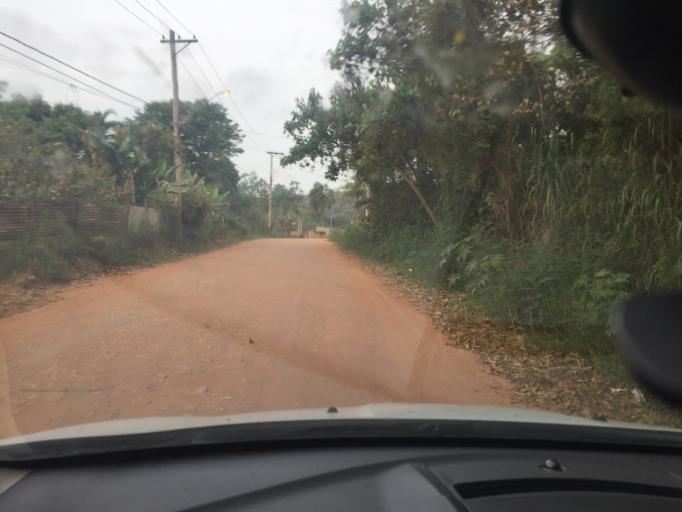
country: BR
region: Sao Paulo
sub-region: Campo Limpo Paulista
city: Campo Limpo Paulista
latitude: -23.1900
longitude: -46.7890
